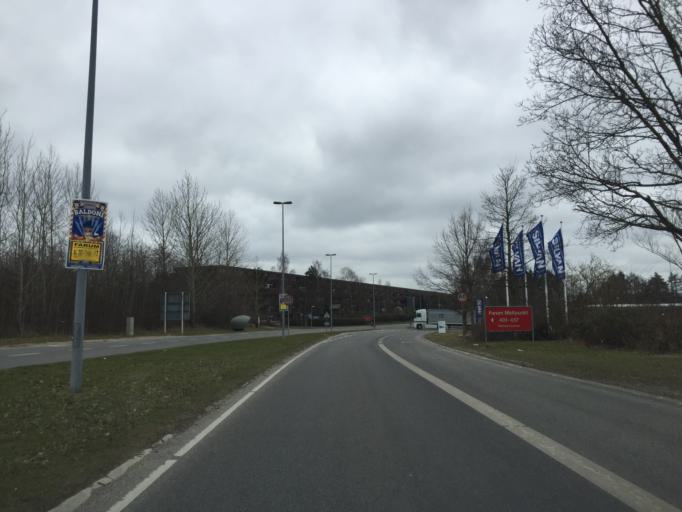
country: DK
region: Capital Region
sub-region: Fureso Kommune
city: Farum
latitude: 55.8229
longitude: 12.3742
